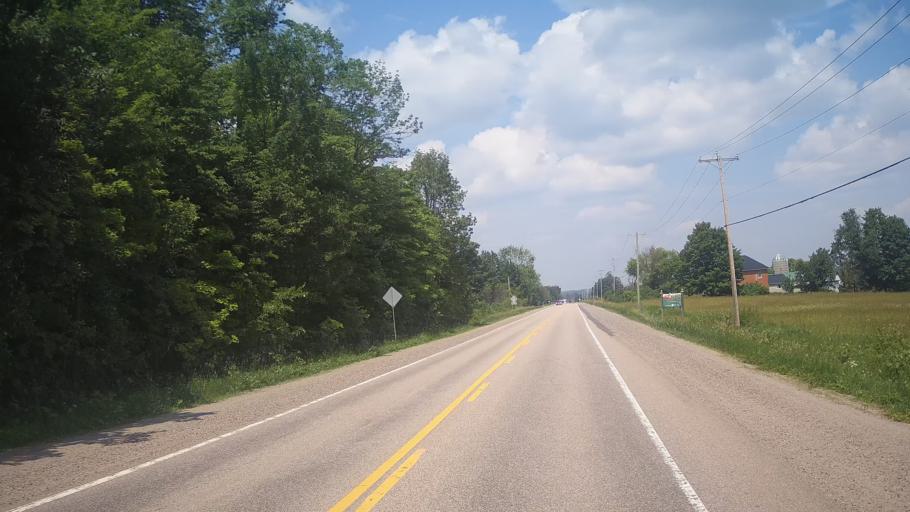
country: CA
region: Quebec
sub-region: Outaouais
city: Shawville
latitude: 45.5763
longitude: -76.4481
